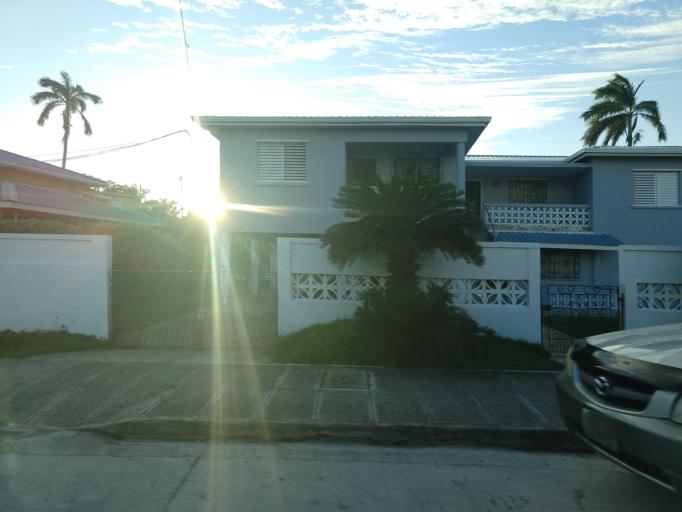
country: BZ
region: Belize
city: Belize City
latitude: 17.5106
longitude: -88.1876
